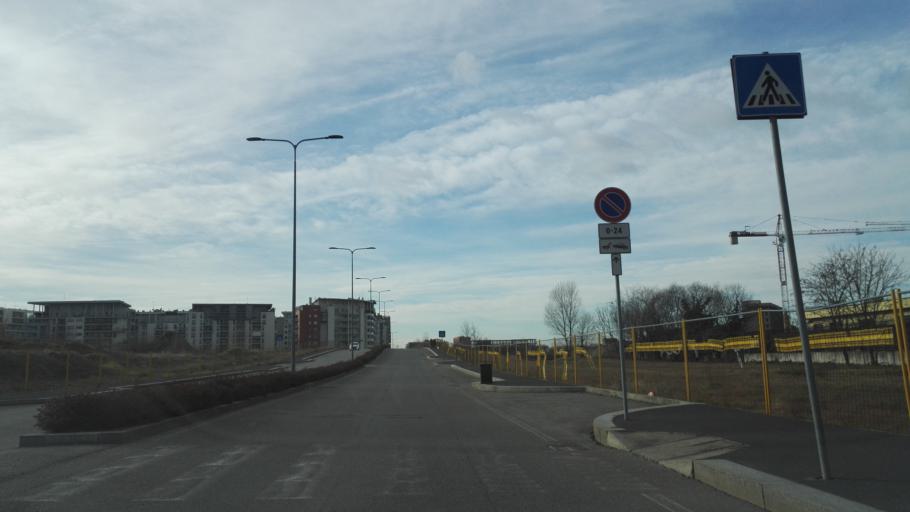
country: IT
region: Lombardy
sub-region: Citta metropolitana di Milano
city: Chiaravalle
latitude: 45.4416
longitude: 9.2451
